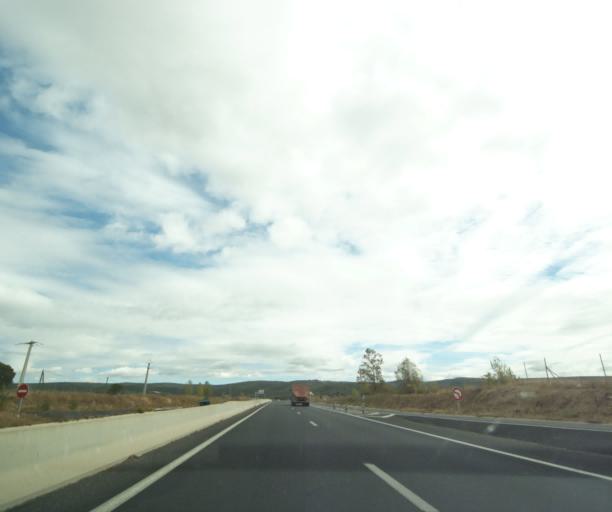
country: FR
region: Languedoc-Roussillon
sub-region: Departement de l'Herault
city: Gignac
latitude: 43.6405
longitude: 3.5737
